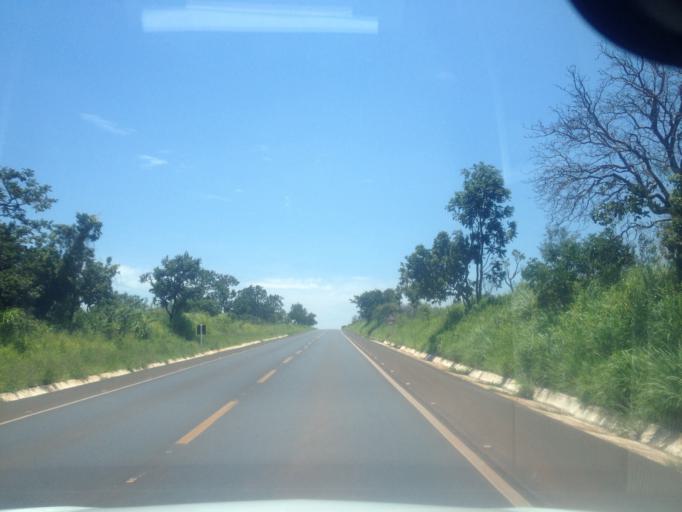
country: BR
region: Minas Gerais
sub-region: Monte Alegre De Minas
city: Monte Alegre de Minas
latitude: -18.8800
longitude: -49.1426
